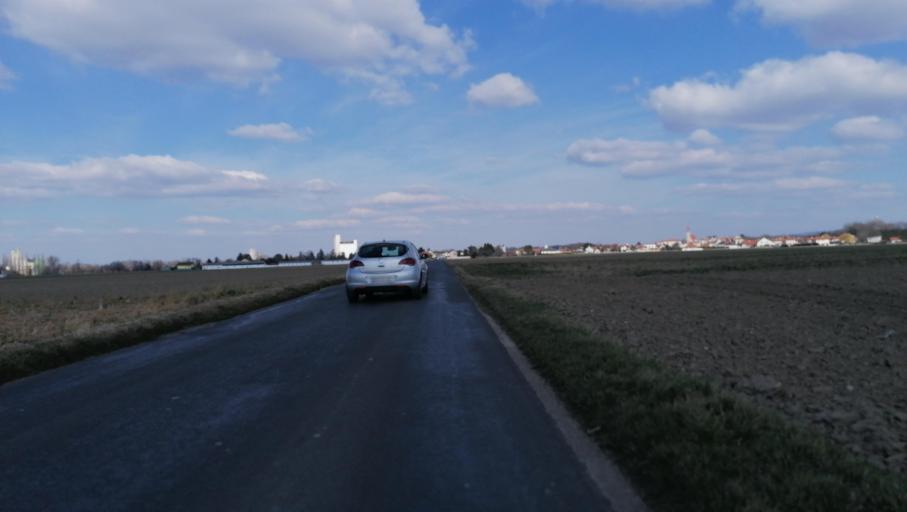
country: AT
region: Lower Austria
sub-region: Politischer Bezirk Wiener Neustadt
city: Lichtenworth
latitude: 47.8269
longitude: 16.2817
